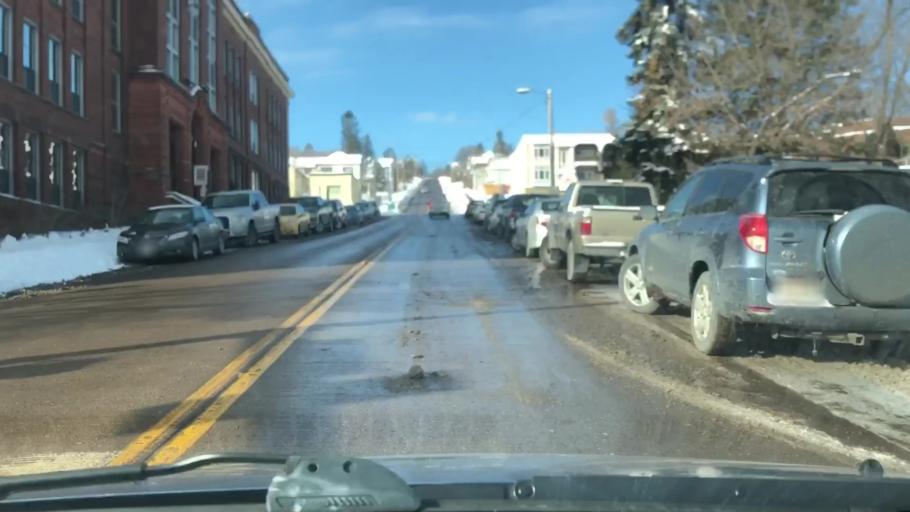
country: US
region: Minnesota
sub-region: Saint Louis County
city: Duluth
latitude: 46.7890
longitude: -92.1015
